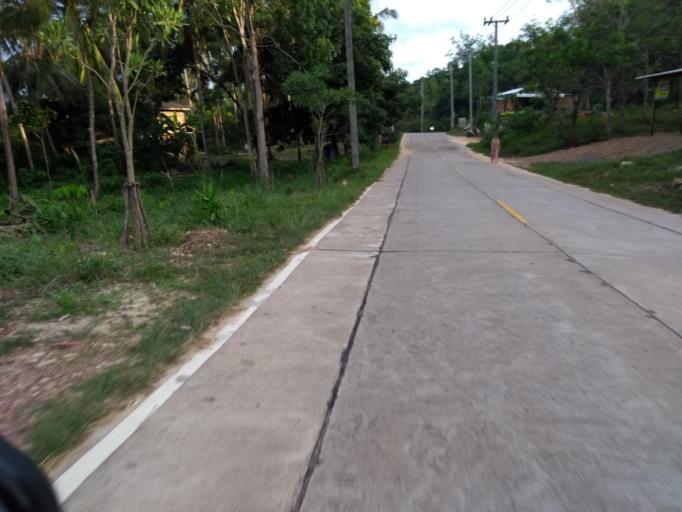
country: TH
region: Trat
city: Ko Kut
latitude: 11.6286
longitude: 102.5464
